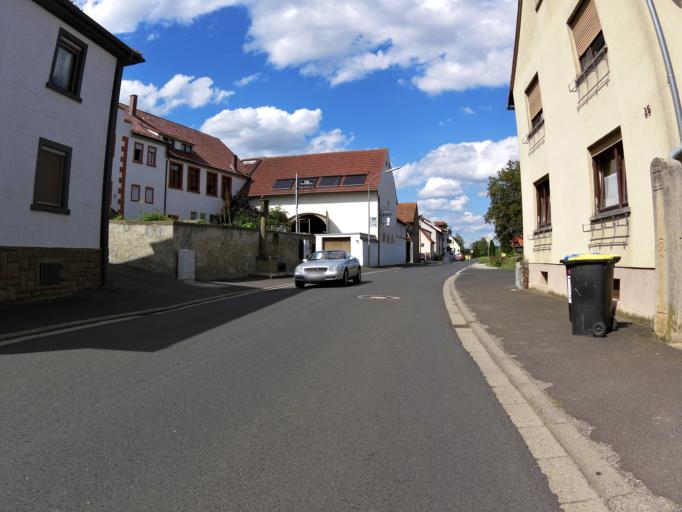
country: DE
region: Bavaria
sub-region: Regierungsbezirk Unterfranken
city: Bergrheinfeld
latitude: 49.9751
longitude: 10.1739
